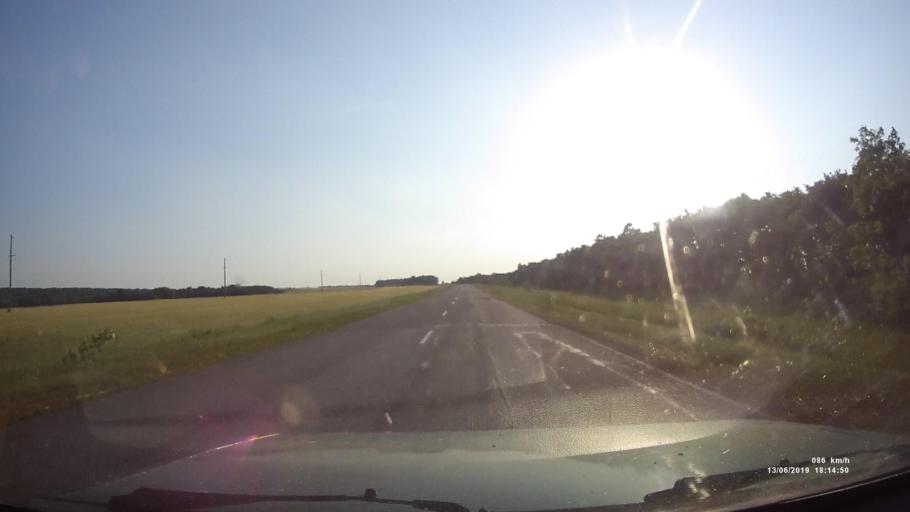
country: RU
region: Rostov
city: Kazanskaya
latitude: 49.9329
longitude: 41.3685
